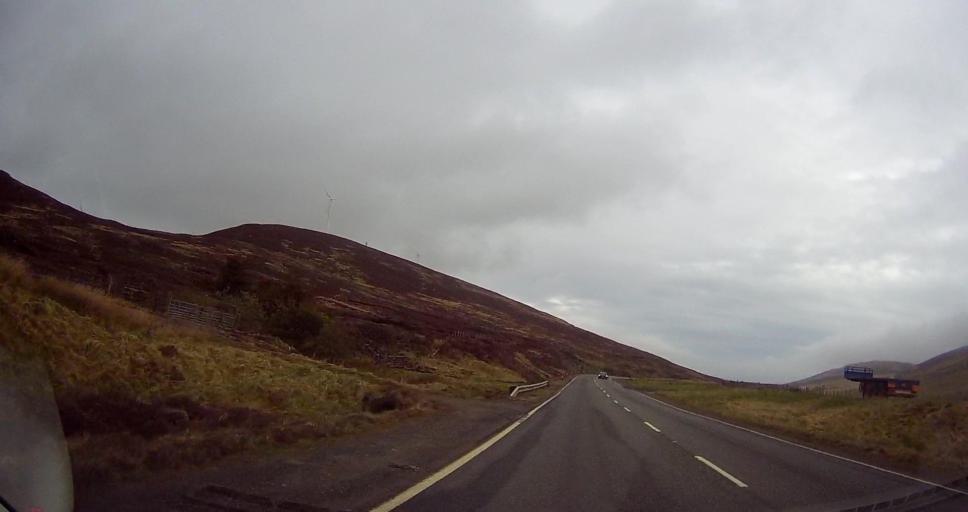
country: GB
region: Scotland
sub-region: Shetland Islands
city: Lerwick
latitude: 60.1555
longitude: -1.2346
